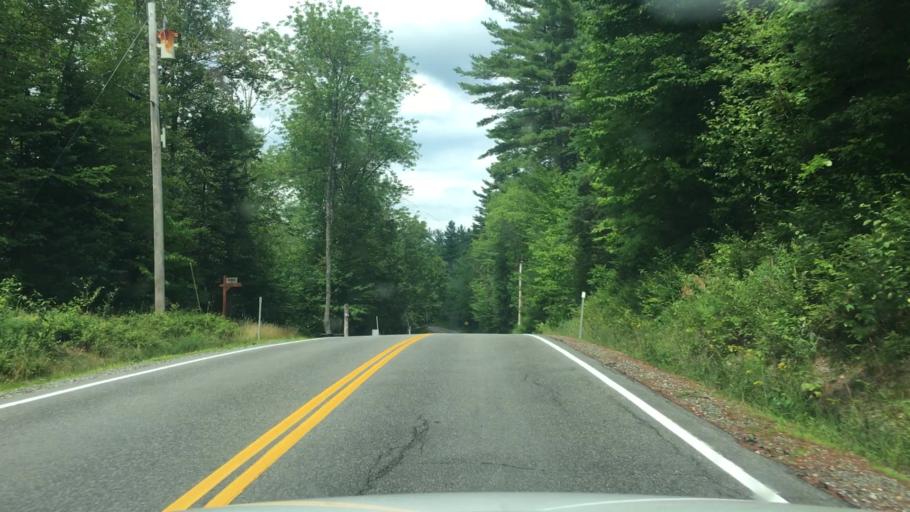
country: US
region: New Hampshire
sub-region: Coos County
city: Whitefield
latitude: 44.3188
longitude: -71.6534
